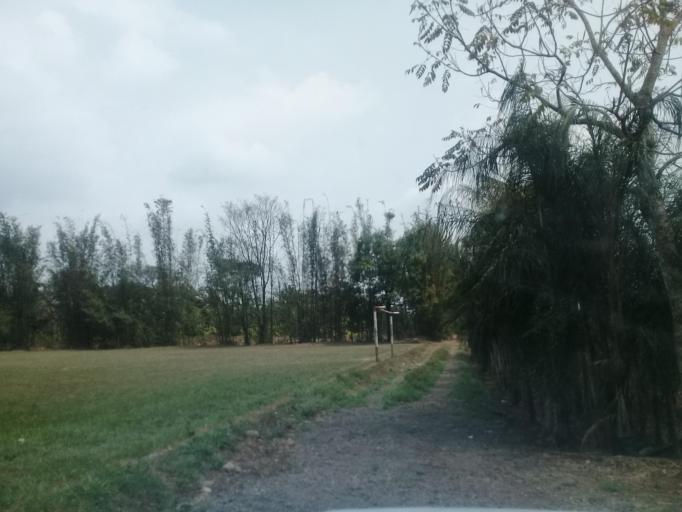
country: MX
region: Veracruz
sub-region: Cordoba
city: Fredepo
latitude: 18.8645
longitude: -96.9922
